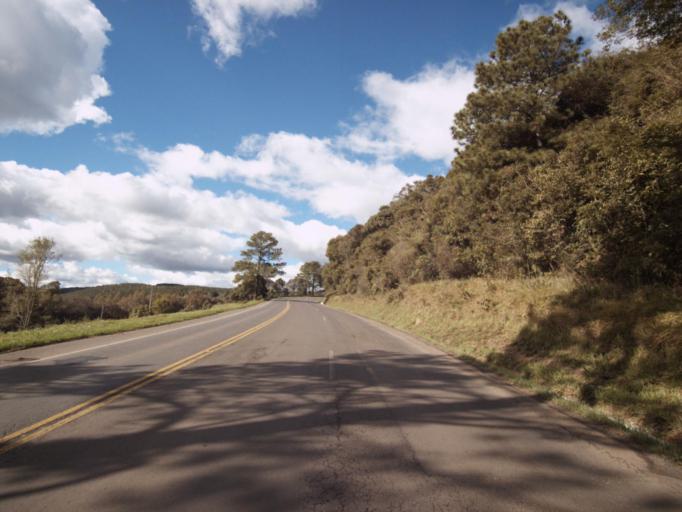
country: BR
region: Santa Catarina
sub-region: Joacaba
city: Joacaba
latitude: -27.0615
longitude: -51.6724
